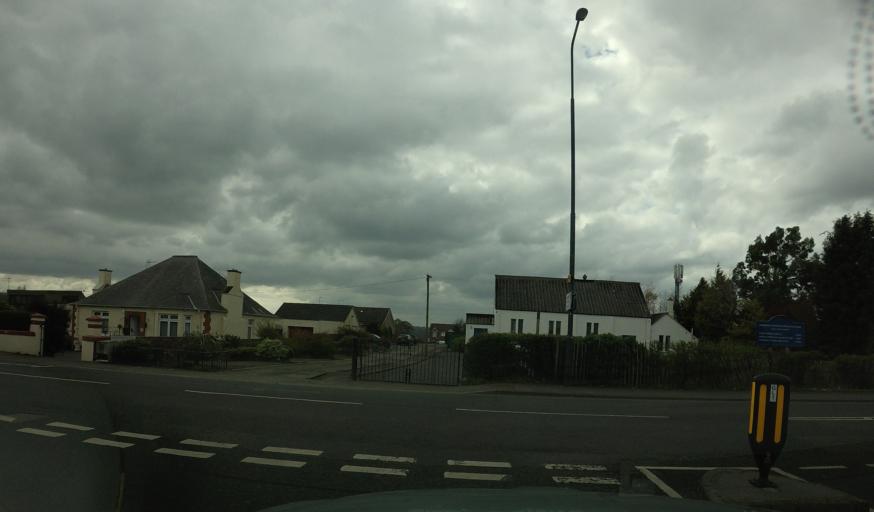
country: GB
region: Scotland
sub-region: Midlothian
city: Gorebridge
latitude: 55.8442
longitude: -3.0493
